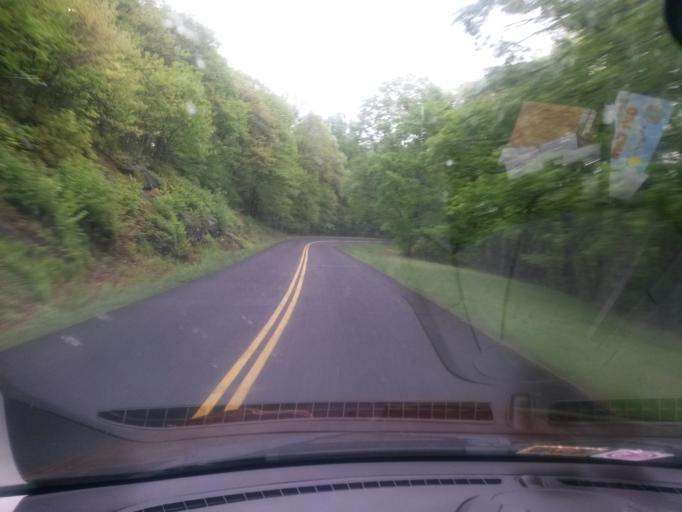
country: US
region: Virginia
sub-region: Floyd County
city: Floyd
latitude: 36.8171
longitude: -80.3458
